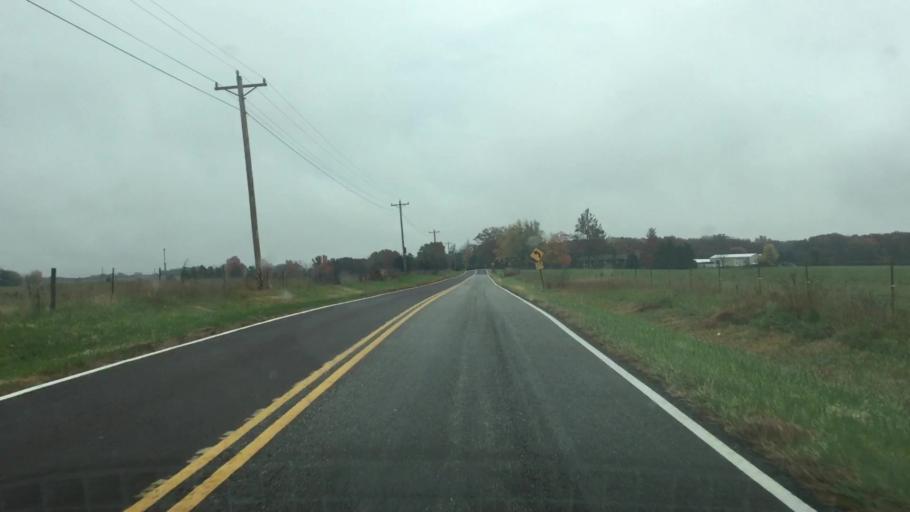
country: US
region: Missouri
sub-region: Callaway County
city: Fulton
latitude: 38.8282
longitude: -91.9148
